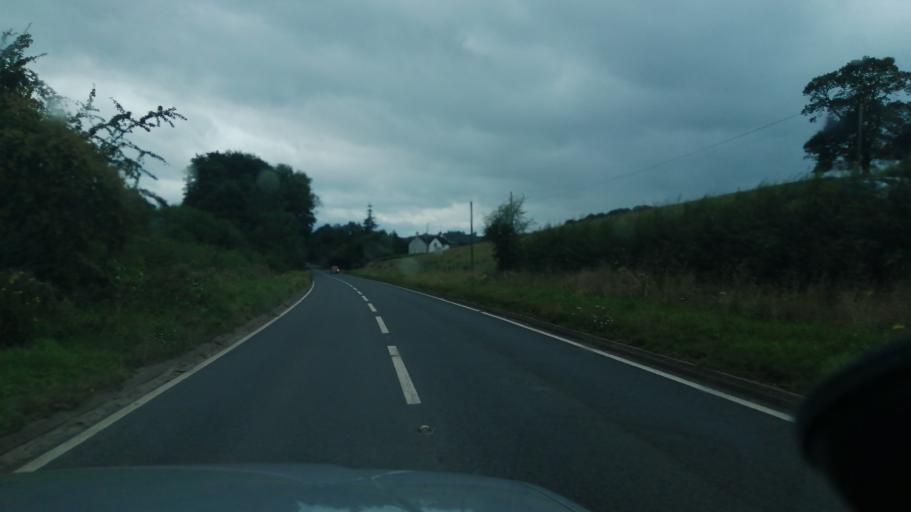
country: GB
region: Wales
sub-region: Monmouthshire
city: Grosmont
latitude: 51.9507
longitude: -2.8681
